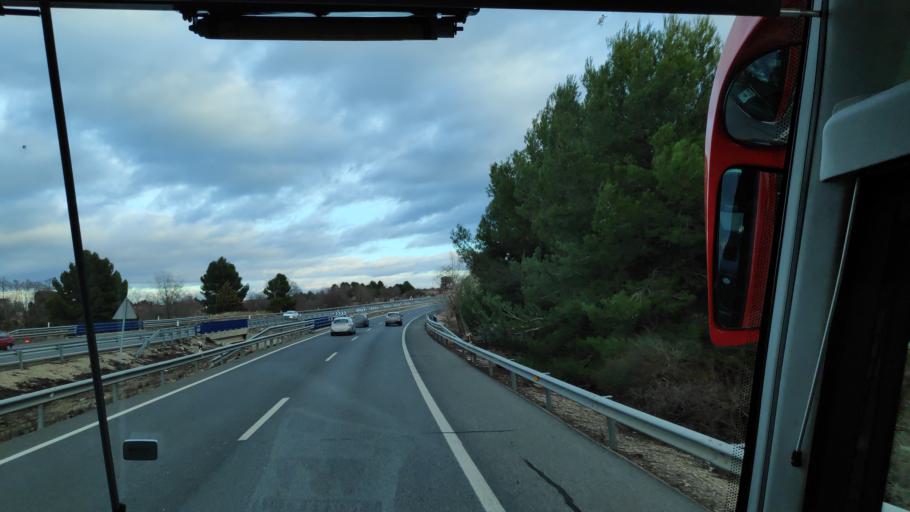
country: ES
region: Madrid
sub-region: Provincia de Madrid
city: Villarejo de Salvanes
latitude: 40.1631
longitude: -3.2688
